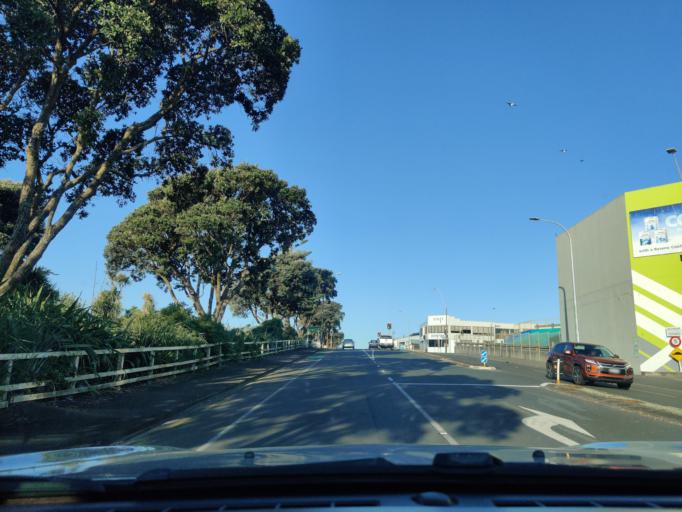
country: NZ
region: Taranaki
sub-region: New Plymouth District
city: New Plymouth
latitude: -39.0558
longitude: 174.0740
